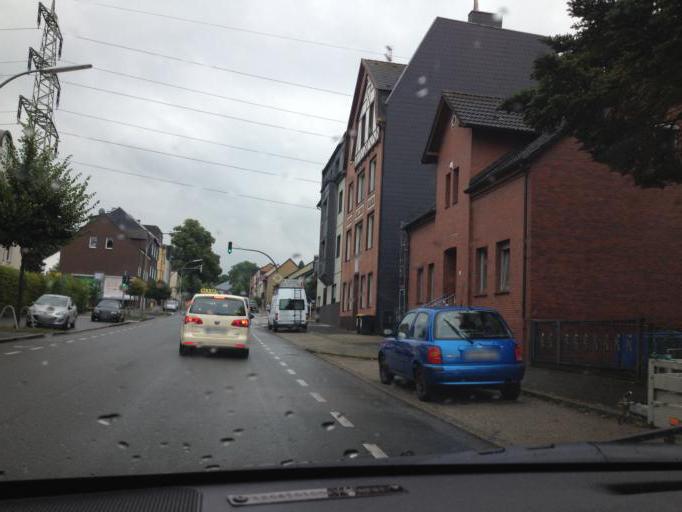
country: DE
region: North Rhine-Westphalia
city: Schwerte
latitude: 51.4811
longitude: 7.5262
